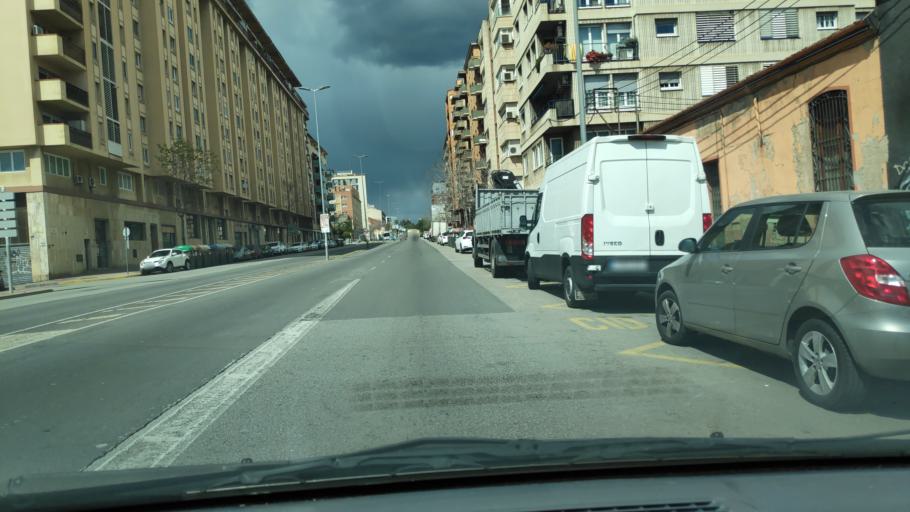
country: ES
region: Catalonia
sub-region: Provincia de Barcelona
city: Sabadell
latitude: 41.5487
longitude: 2.1149
